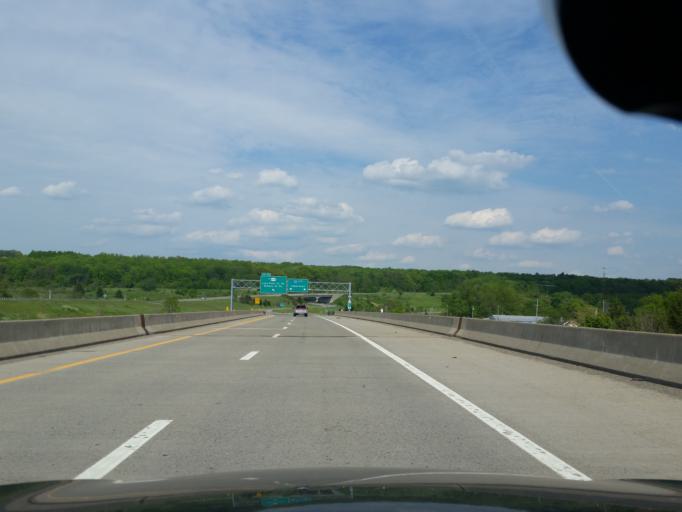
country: US
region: New York
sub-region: Chautauqua County
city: Lakewood
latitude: 42.1524
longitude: -79.3814
